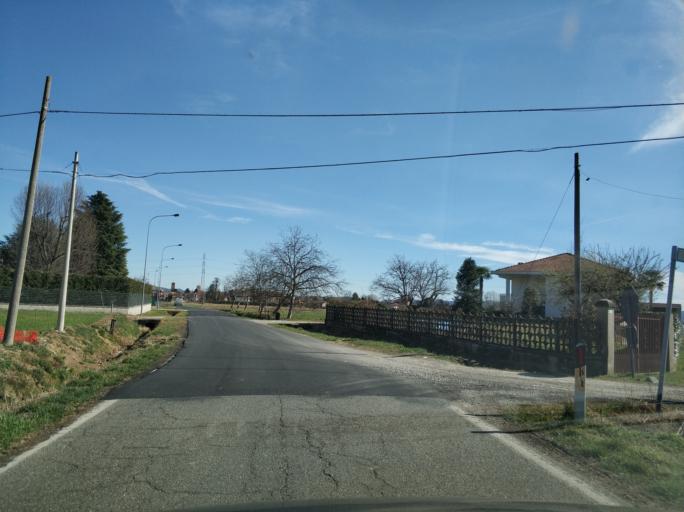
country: IT
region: Piedmont
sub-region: Provincia di Torino
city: Leini
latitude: 45.1889
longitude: 7.7015
